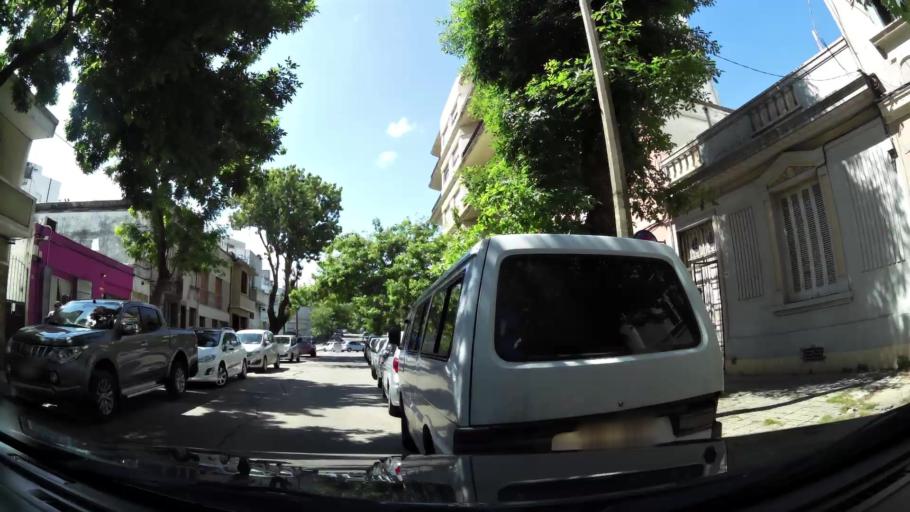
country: UY
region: Montevideo
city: Montevideo
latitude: -34.9119
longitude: -56.1617
